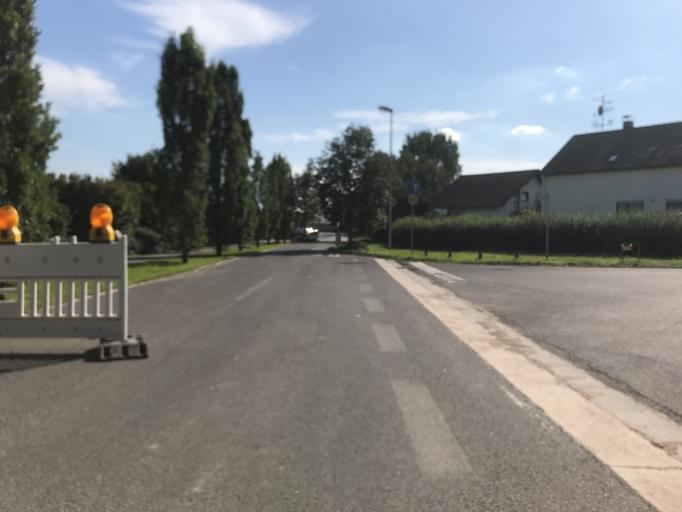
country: DE
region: Hesse
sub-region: Regierungsbezirk Darmstadt
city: Eltville
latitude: 50.0113
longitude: 8.1025
